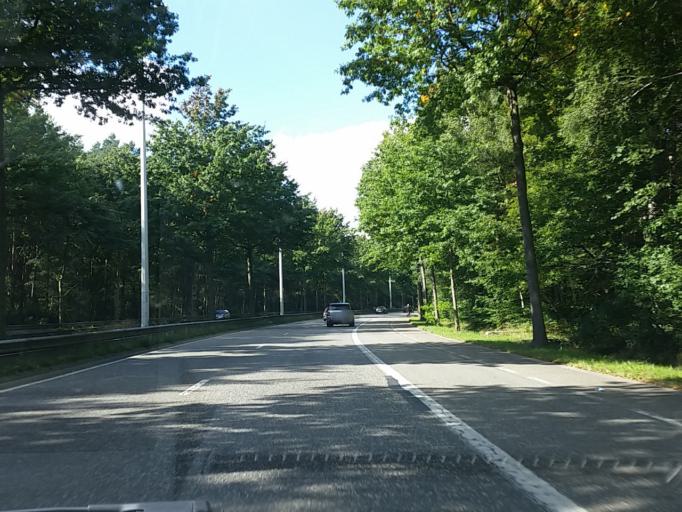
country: BE
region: Flanders
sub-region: Provincie Antwerpen
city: Wijnegem
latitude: 51.2314
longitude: 4.5483
